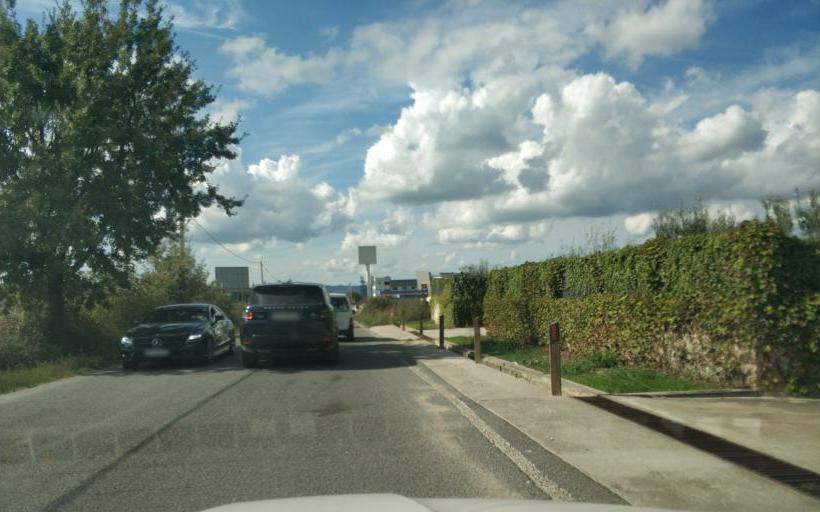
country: AL
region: Durres
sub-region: Rrethi i Krujes
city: Nikel
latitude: 41.4790
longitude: 19.7567
